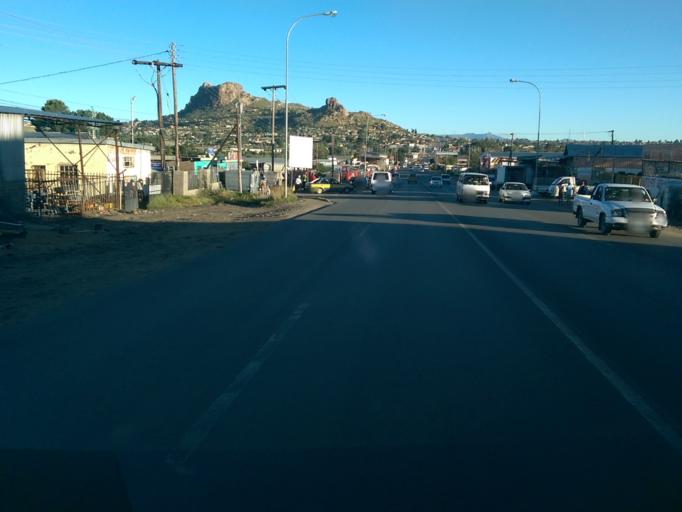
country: LS
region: Maseru
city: Maseru
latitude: -29.3390
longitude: 27.5124
